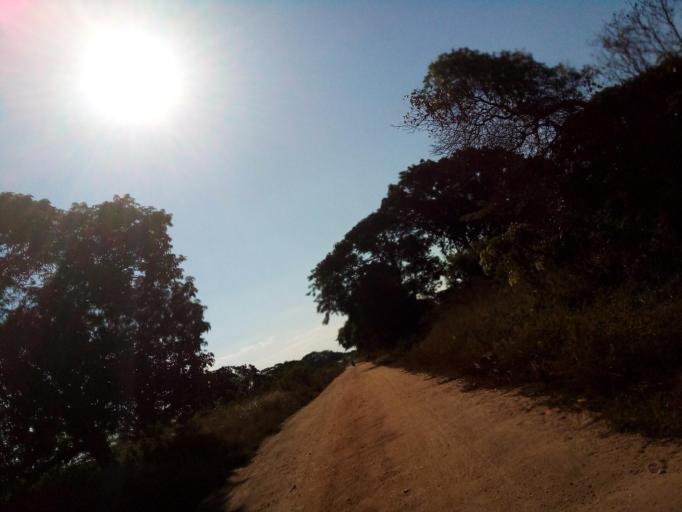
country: MZ
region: Zambezia
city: Quelimane
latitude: -17.5154
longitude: 36.6055
